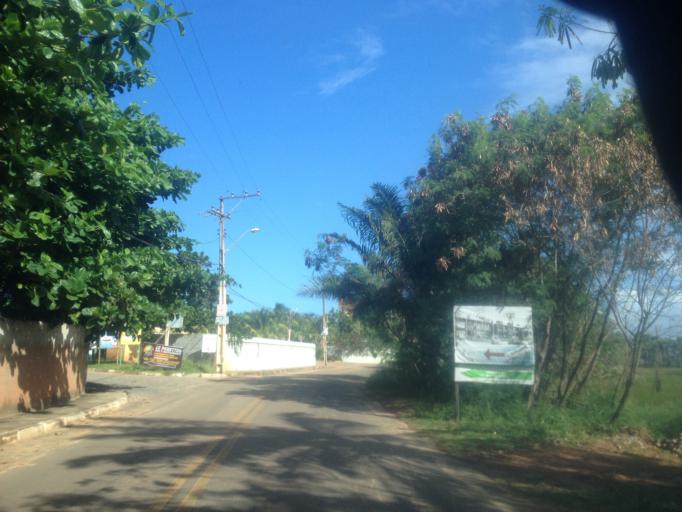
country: BR
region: Bahia
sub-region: Mata De Sao Joao
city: Mata de Sao Joao
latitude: -12.6262
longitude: -38.0484
